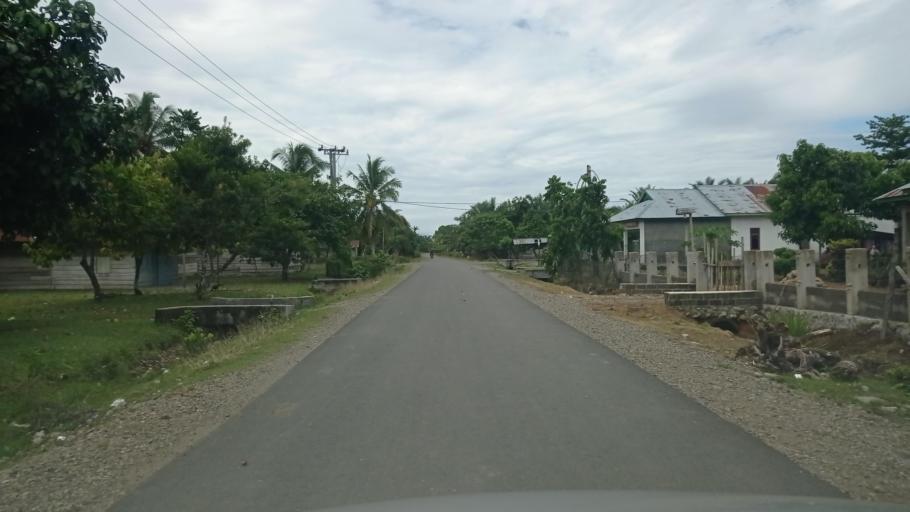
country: ID
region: Jambi
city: Sungai Penuh
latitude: -2.5265
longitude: 101.0813
